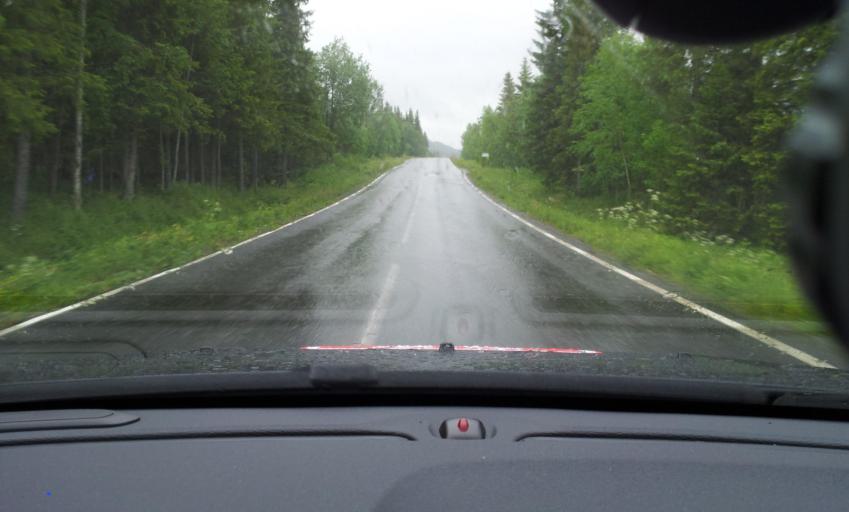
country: SE
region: Jaemtland
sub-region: Are Kommun
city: Are
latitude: 63.3153
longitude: 13.1196
